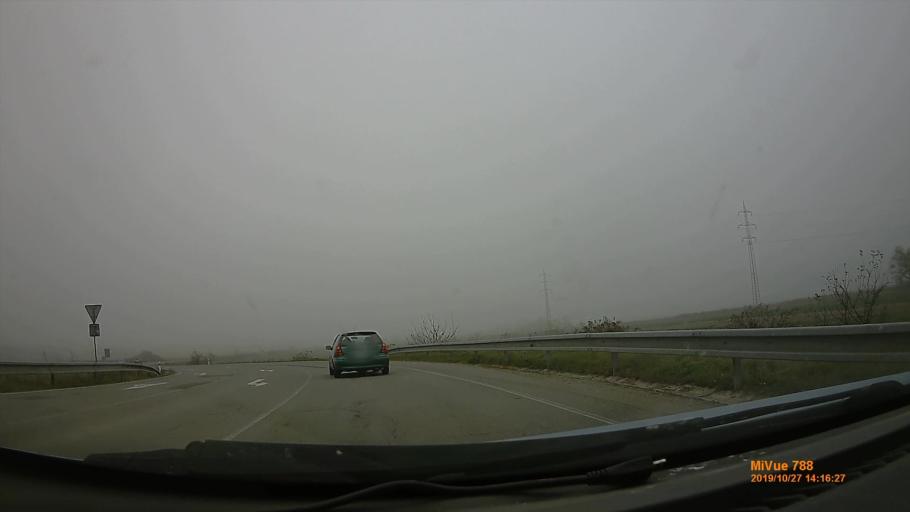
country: CZ
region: Olomoucky
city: Zabreh
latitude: 49.8896
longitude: 16.8924
